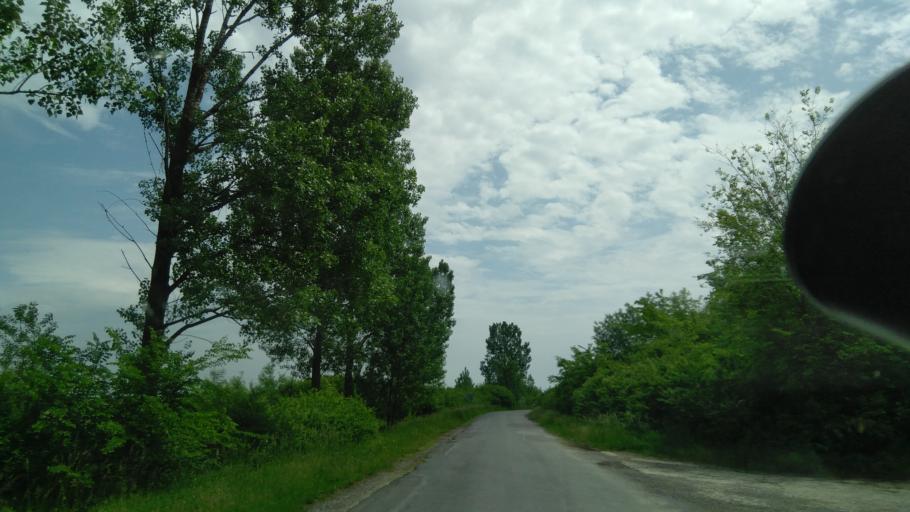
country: HU
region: Hajdu-Bihar
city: Komadi
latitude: 47.0071
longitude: 21.6105
